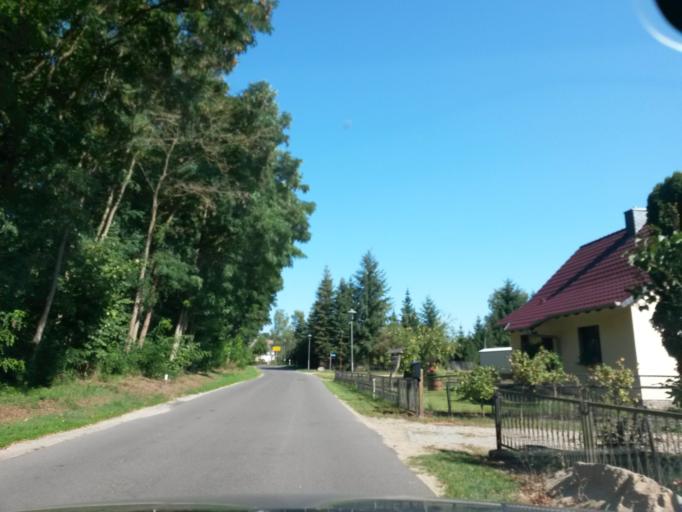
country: DE
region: Brandenburg
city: Lychen
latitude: 53.1437
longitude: 13.3768
